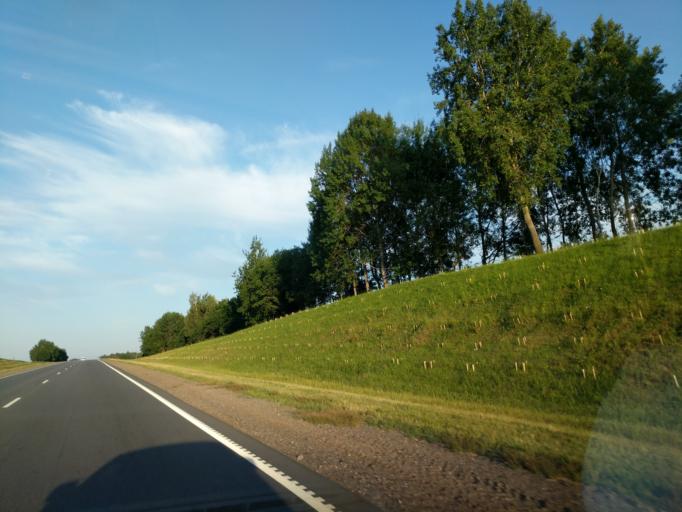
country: BY
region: Minsk
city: Bal'shavik
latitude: 54.0920
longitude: 27.5227
